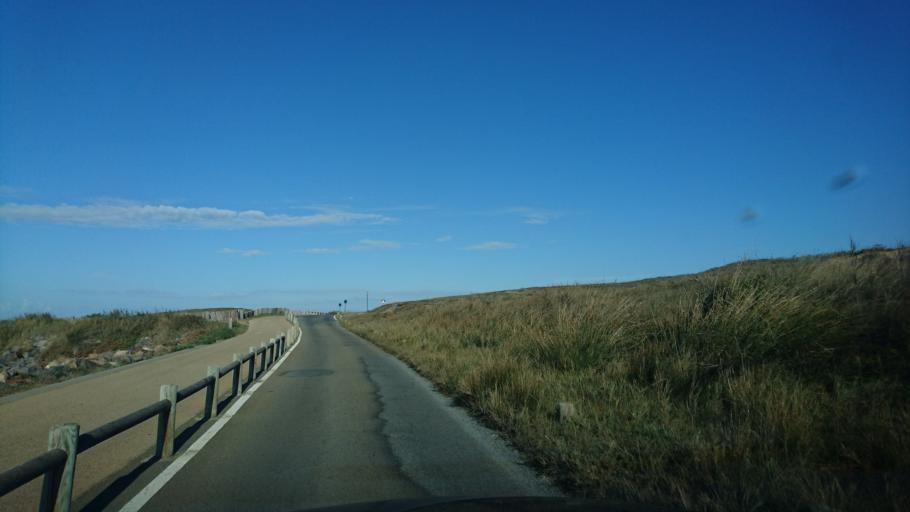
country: FR
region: Pays de la Loire
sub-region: Departement de la Vendee
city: Les Sables-d'Olonne
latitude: 46.5093
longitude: -1.8180
